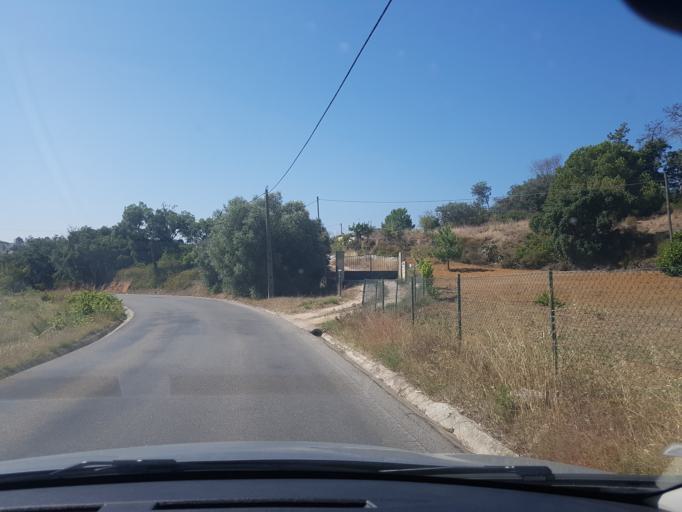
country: PT
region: Faro
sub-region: Lagoa
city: Carvoeiro
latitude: 37.1051
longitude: -8.4303
